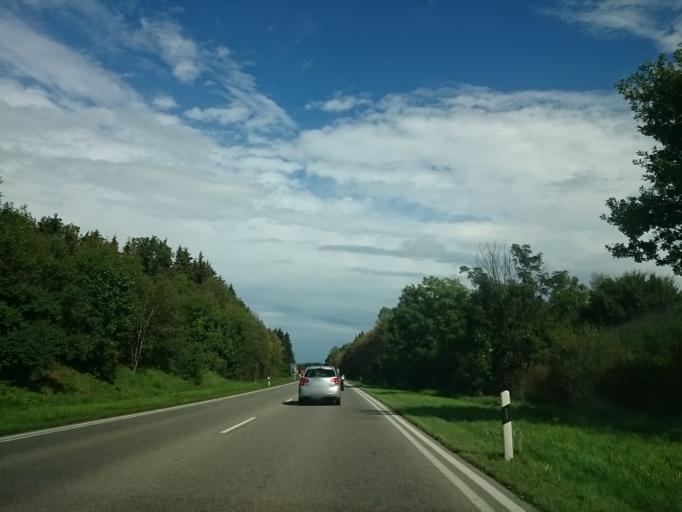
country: DE
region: Bavaria
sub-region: Swabia
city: Mauerstetten
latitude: 47.8875
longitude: 10.6470
